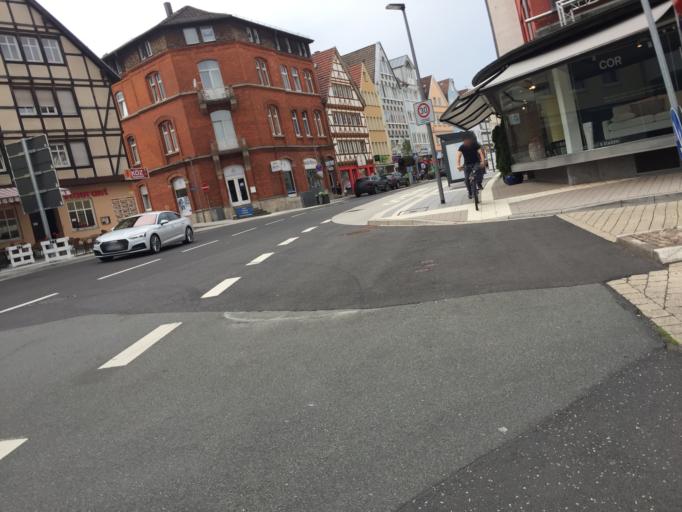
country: DE
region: Hesse
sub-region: Regierungsbezirk Kassel
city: Bad Hersfeld
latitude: 50.8669
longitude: 9.7118
